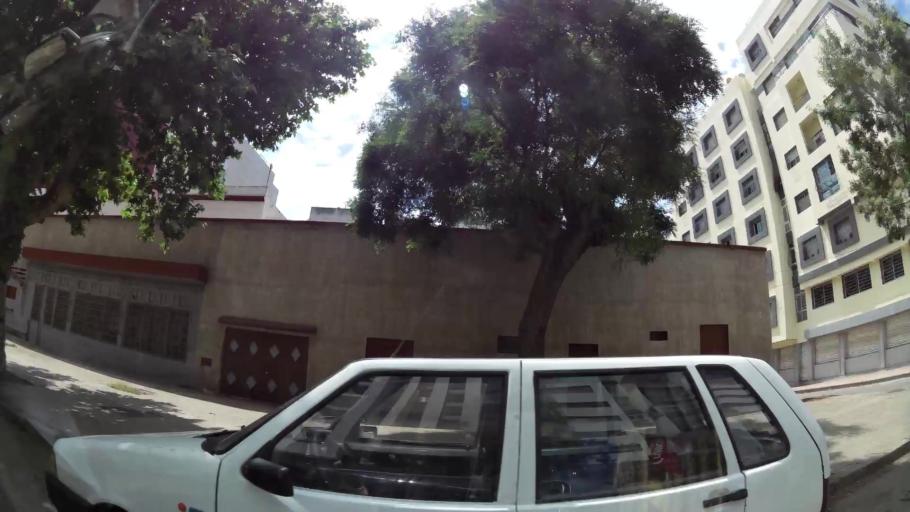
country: MA
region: Gharb-Chrarda-Beni Hssen
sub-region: Kenitra Province
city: Kenitra
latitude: 34.2610
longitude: -6.5885
